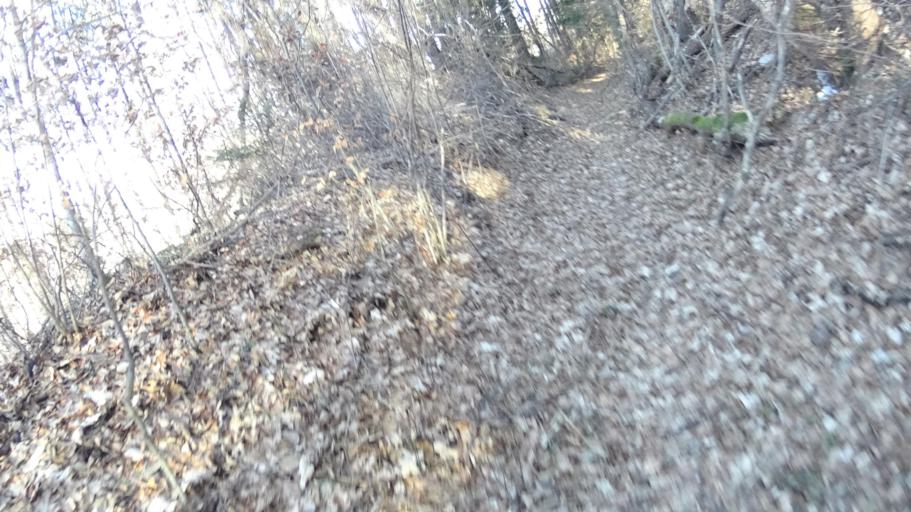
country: HU
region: Heves
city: Szilvasvarad
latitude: 48.0916
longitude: 20.4778
